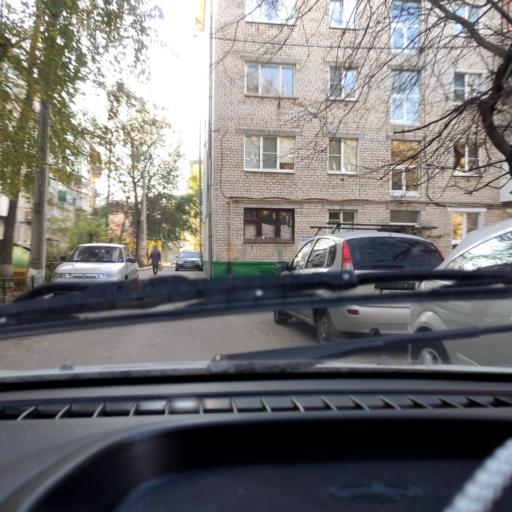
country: RU
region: Samara
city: Tol'yatti
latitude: 53.5169
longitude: 49.4182
